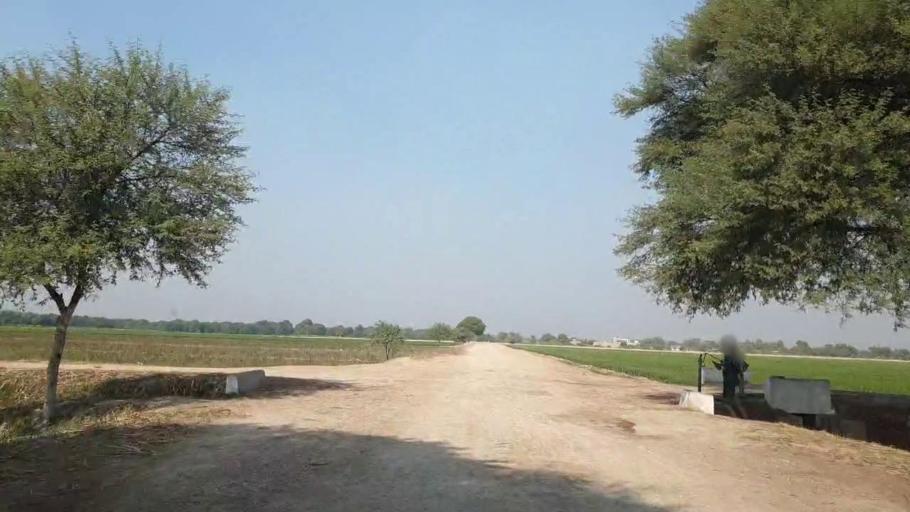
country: PK
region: Sindh
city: Tando Allahyar
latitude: 25.5002
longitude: 68.8340
